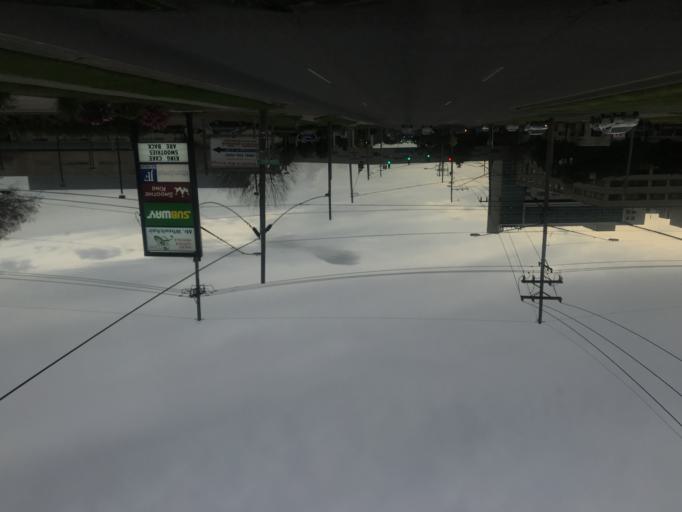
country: US
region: Louisiana
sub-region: Jefferson Parish
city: Jefferson
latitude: 29.9625
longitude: -90.1425
